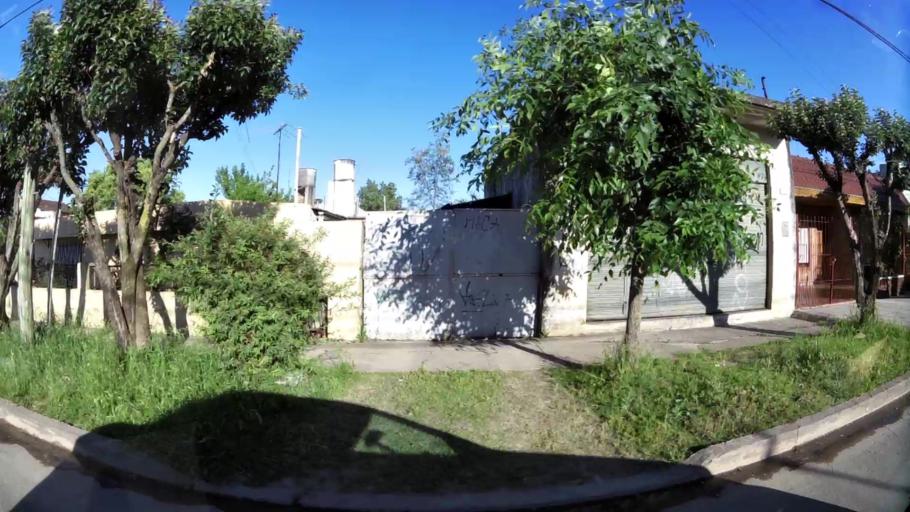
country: AR
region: Buenos Aires
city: Ituzaingo
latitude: -34.6871
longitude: -58.6392
